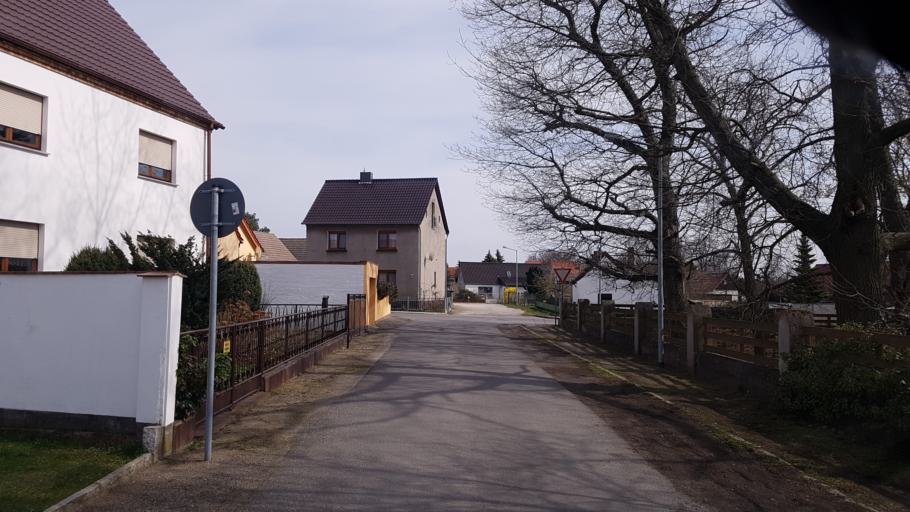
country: DE
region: Brandenburg
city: Lauchhammer
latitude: 51.5150
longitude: 13.7010
